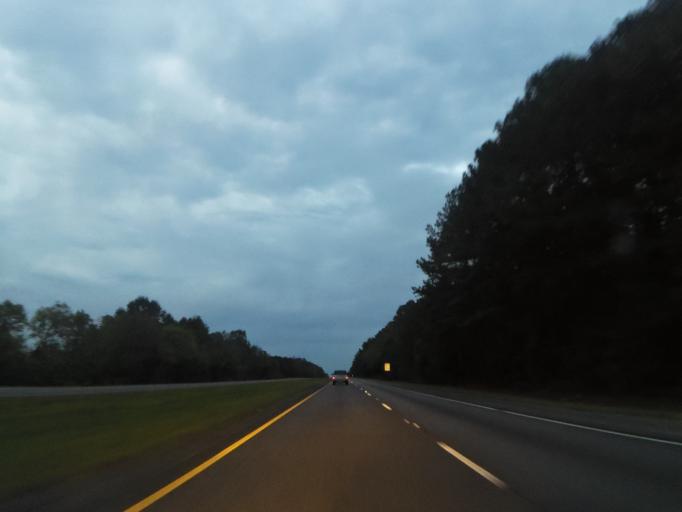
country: US
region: Alabama
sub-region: Etowah County
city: Whitesboro
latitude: 34.1762
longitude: -85.9641
